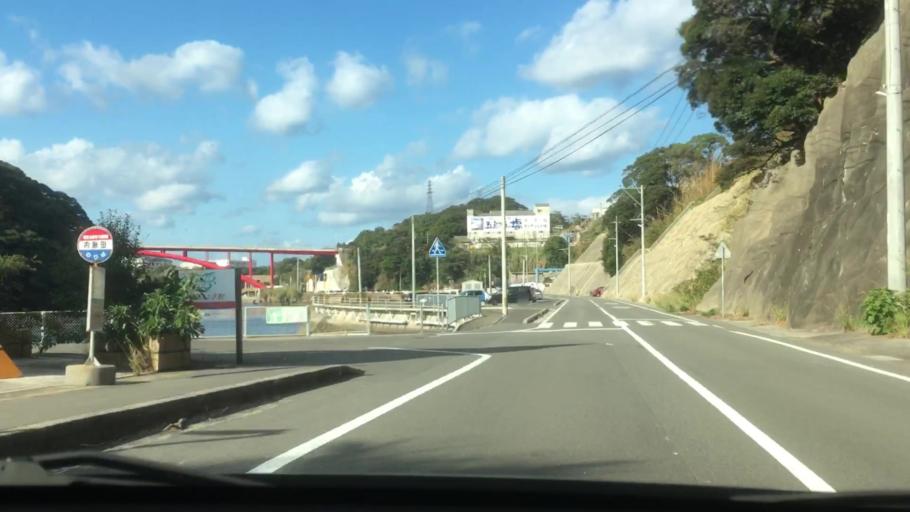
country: JP
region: Nagasaki
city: Sasebo
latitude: 33.0241
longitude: 129.5756
